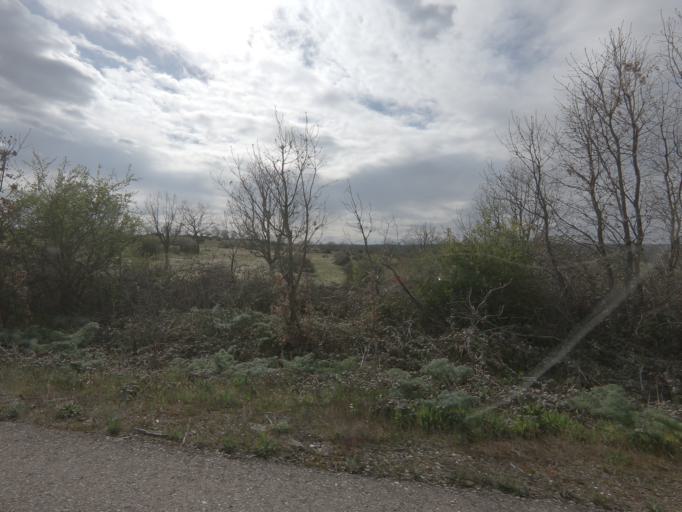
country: ES
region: Castille and Leon
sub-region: Provincia de Salamanca
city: Robleda
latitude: 40.4235
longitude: -6.5997
